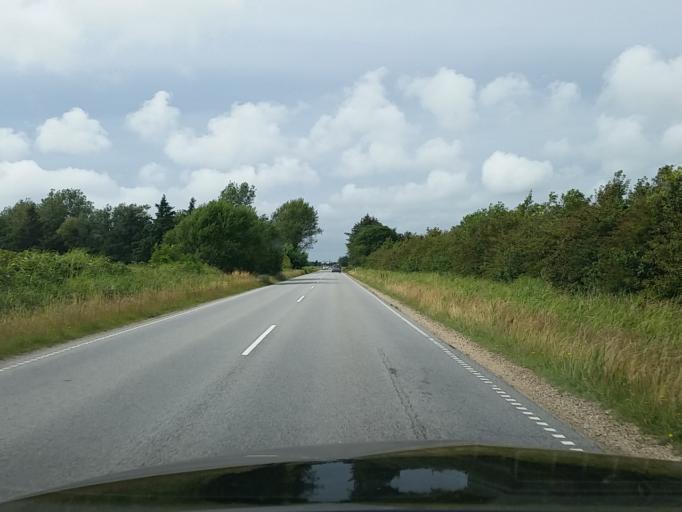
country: DK
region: South Denmark
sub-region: Varde Kommune
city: Oksbol
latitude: 55.7959
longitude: 8.2336
